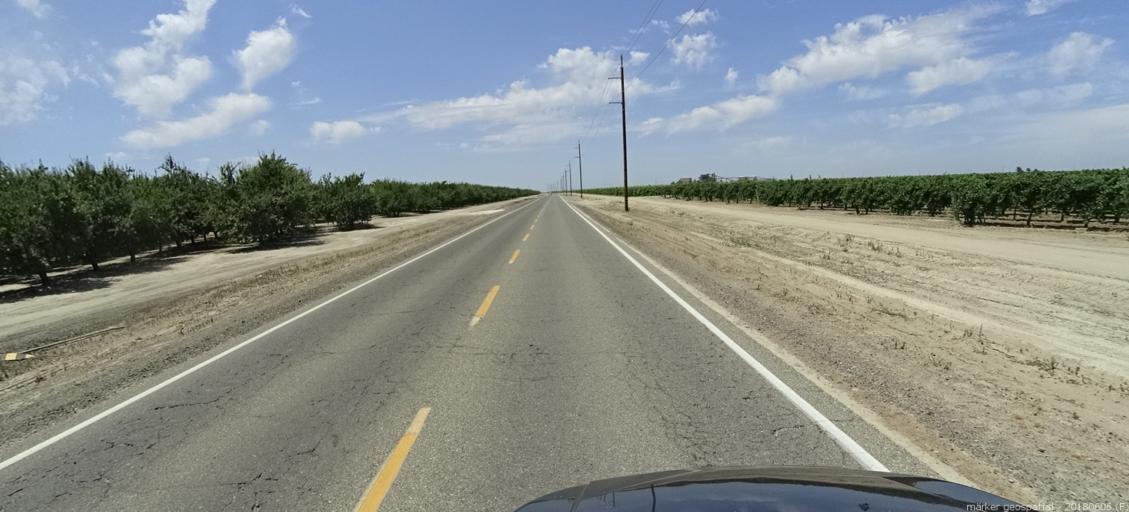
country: US
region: California
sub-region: Fresno County
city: Mendota
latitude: 36.8543
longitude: -120.3267
